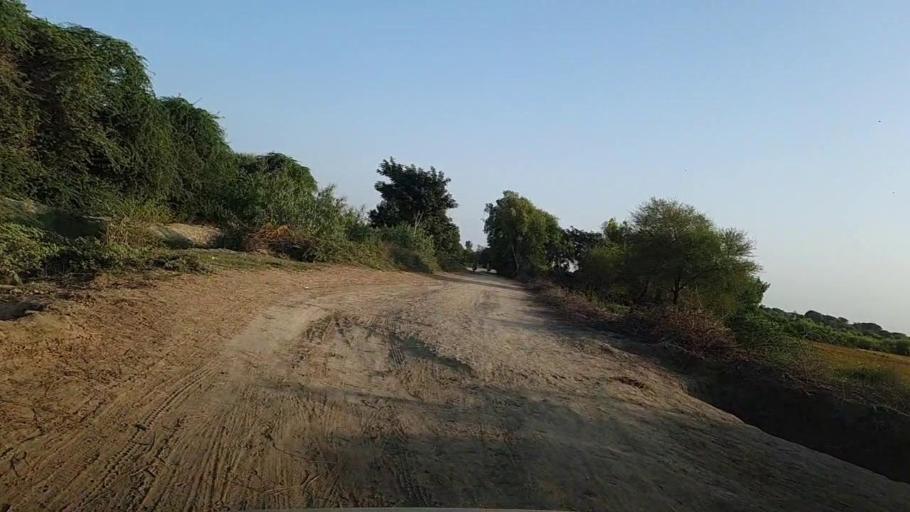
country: PK
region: Sindh
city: Kario
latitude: 24.6992
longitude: 68.6706
